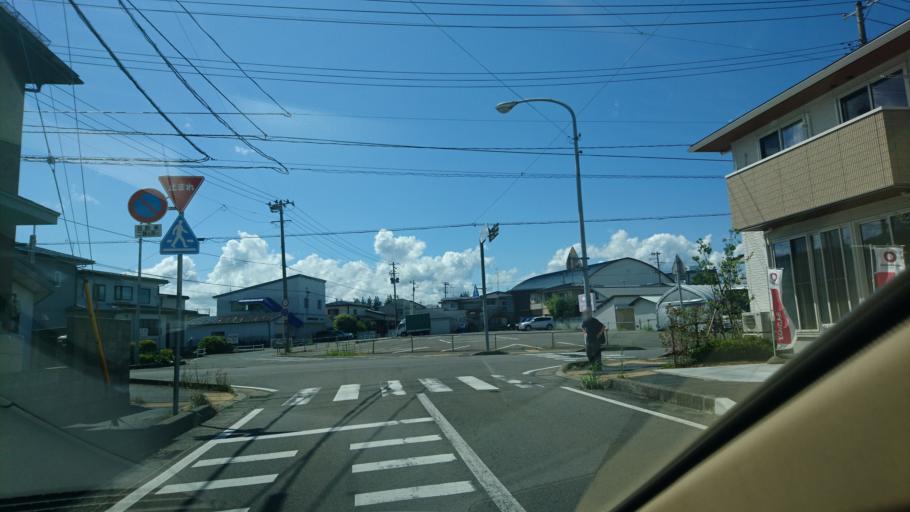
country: JP
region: Iwate
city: Kitakami
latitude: 39.2872
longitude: 141.1094
